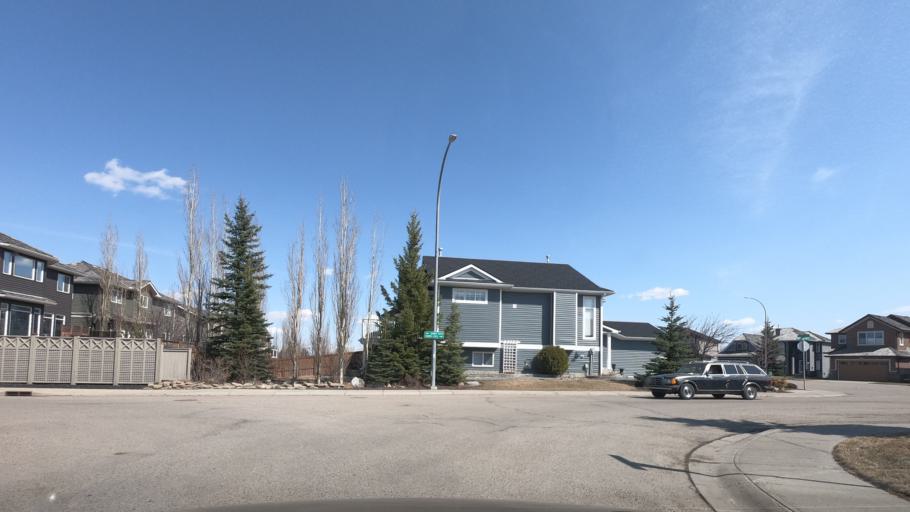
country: CA
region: Alberta
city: Airdrie
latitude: 51.2982
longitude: -114.0470
